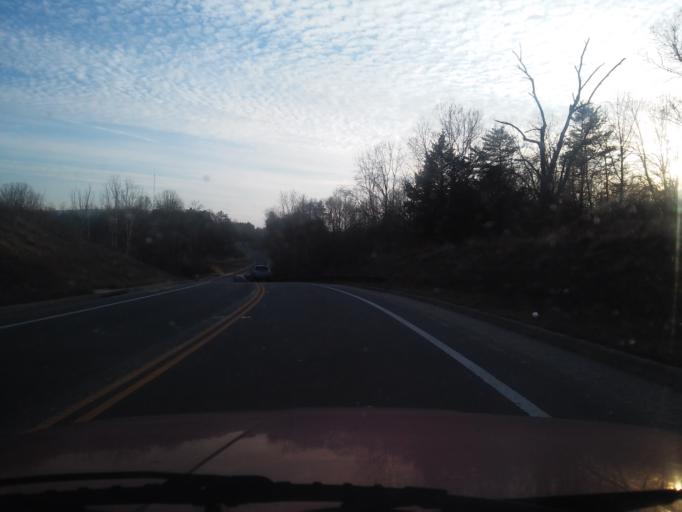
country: US
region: Virginia
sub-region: City of Charlottesville
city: Charlottesville
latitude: 38.0599
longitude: -78.4663
